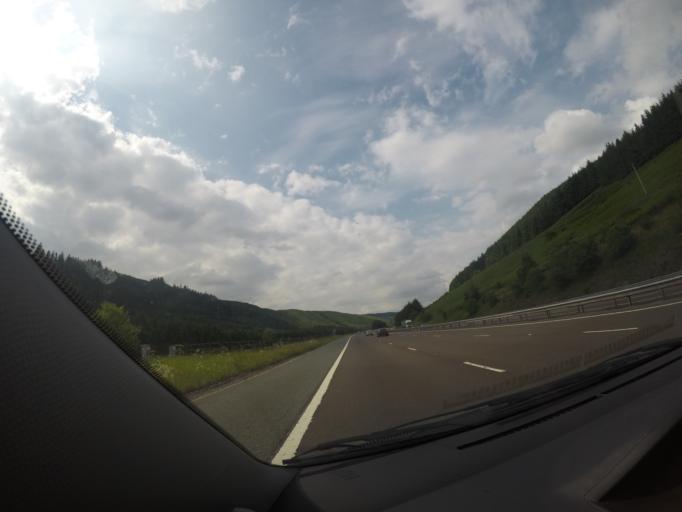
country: GB
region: Scotland
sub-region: Dumfries and Galloway
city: Moffat
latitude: 55.3767
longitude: -3.5162
